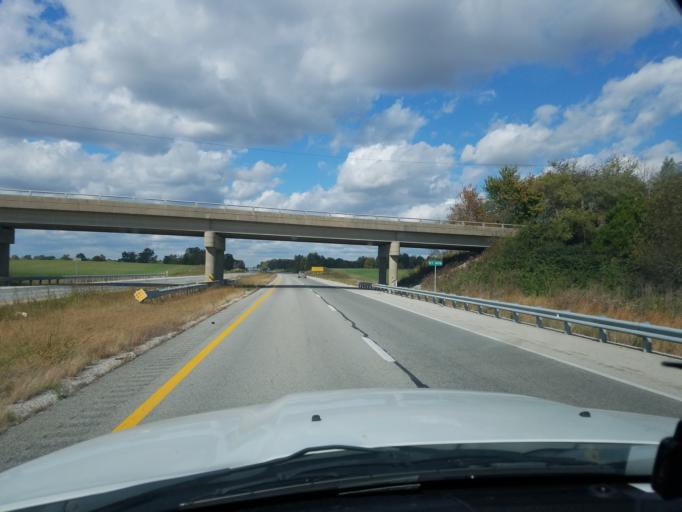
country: US
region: Kentucky
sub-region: Daviess County
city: Masonville
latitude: 37.7173
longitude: -87.0510
